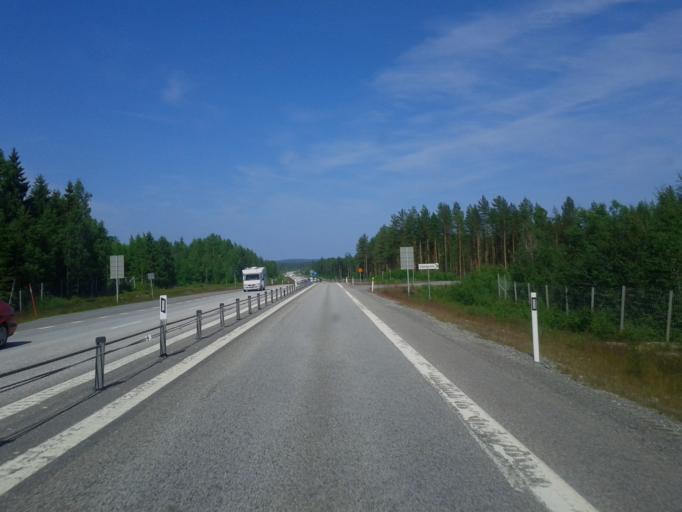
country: SE
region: Vaesterbotten
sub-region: Umea Kommun
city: Hoernefors
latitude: 63.6539
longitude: 19.9525
